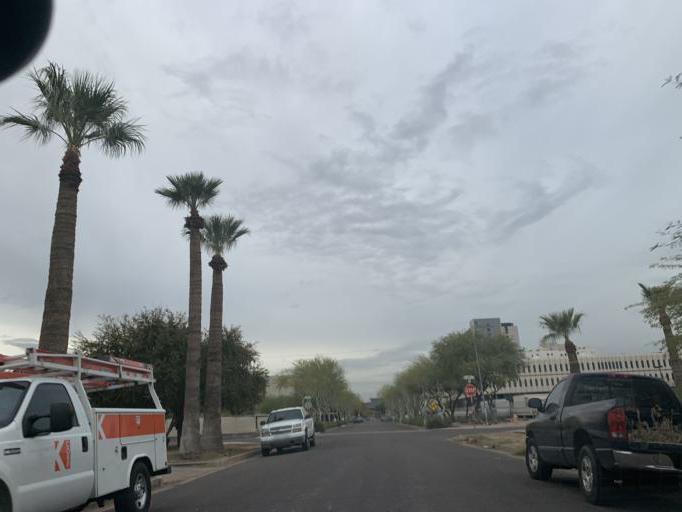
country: US
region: Arizona
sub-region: Maricopa County
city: Phoenix
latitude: 33.4637
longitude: -112.0538
